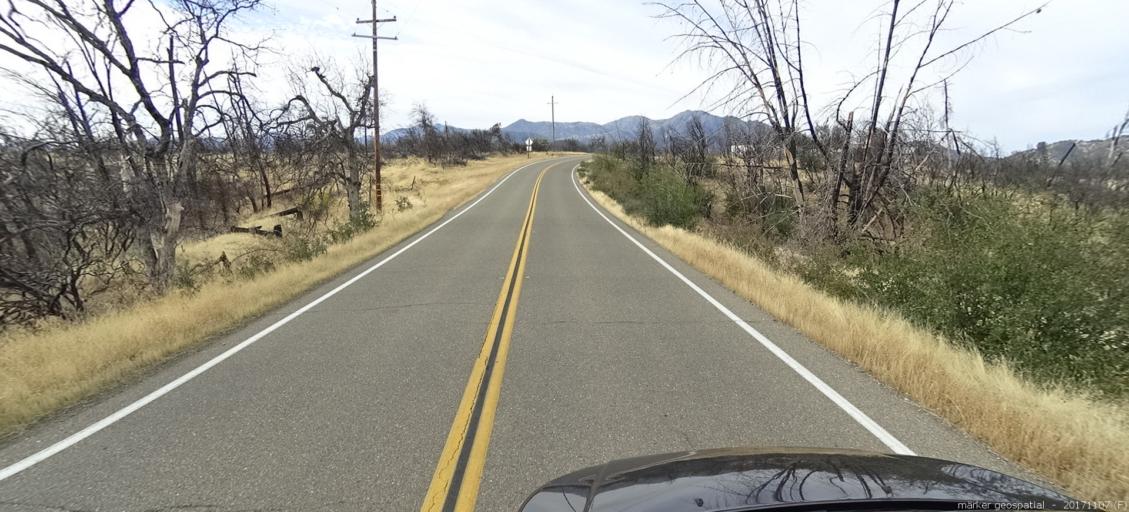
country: US
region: California
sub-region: Shasta County
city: Shasta
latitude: 40.4886
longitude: -122.5128
